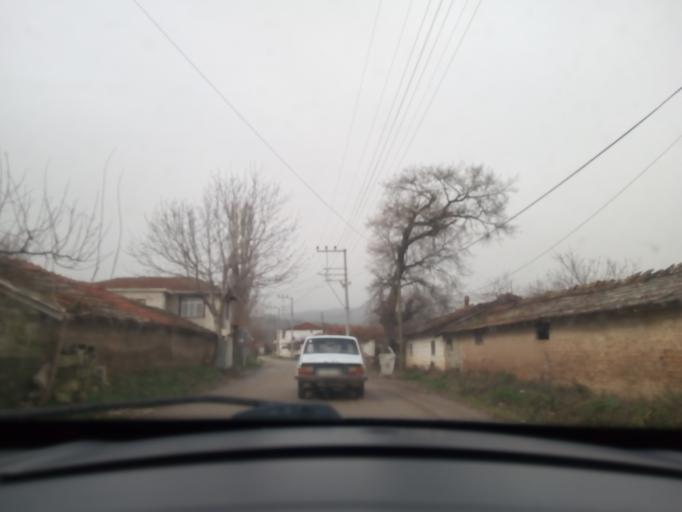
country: TR
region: Balikesir
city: Susurluk
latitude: 39.9218
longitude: 28.1458
